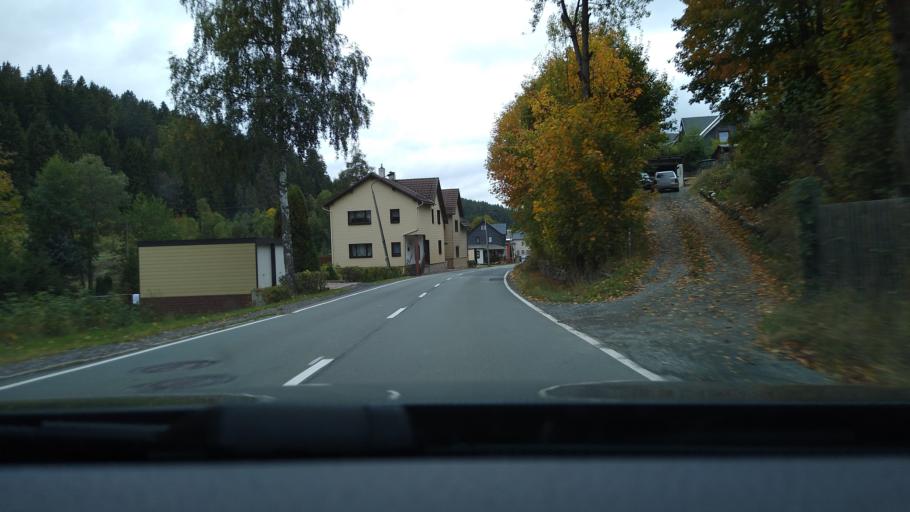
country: DE
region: Thuringia
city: Piesau
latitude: 50.5238
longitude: 11.2194
